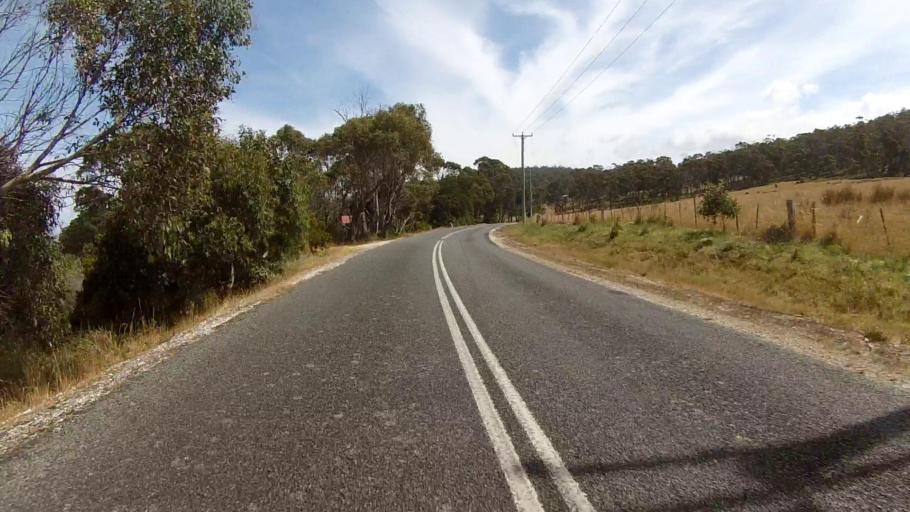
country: AU
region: Tasmania
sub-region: Huon Valley
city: Cygnet
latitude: -43.2783
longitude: 147.1633
